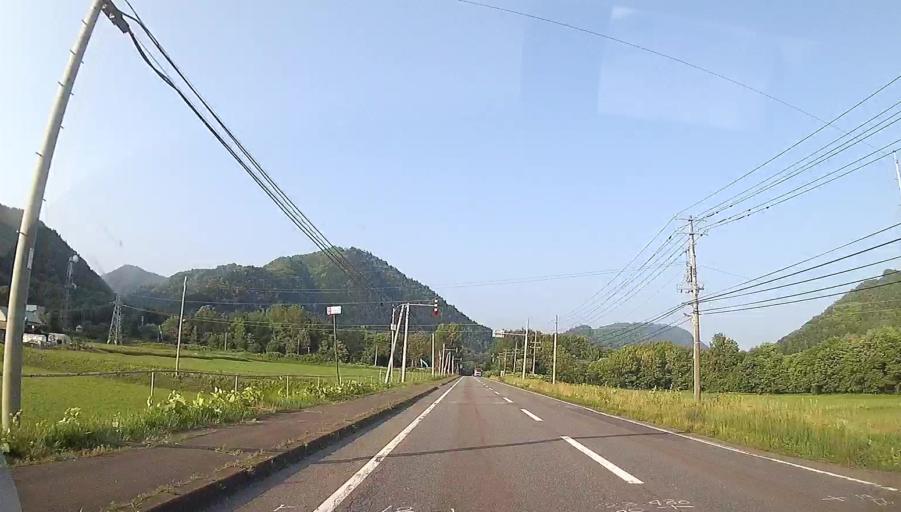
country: JP
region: Hokkaido
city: Shimo-furano
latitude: 42.8899
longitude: 142.4667
